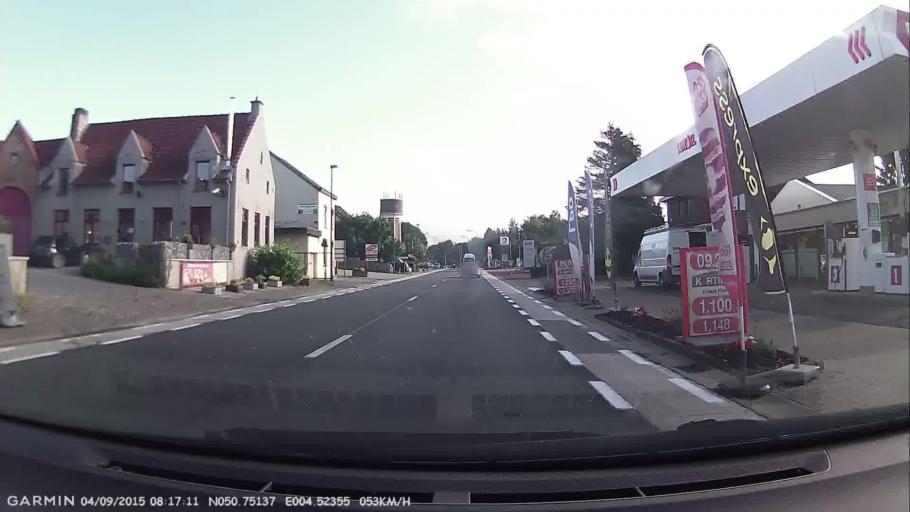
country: BE
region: Flanders
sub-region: Provincie Vlaams-Brabant
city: Overijse
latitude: 50.7515
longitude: 4.5237
